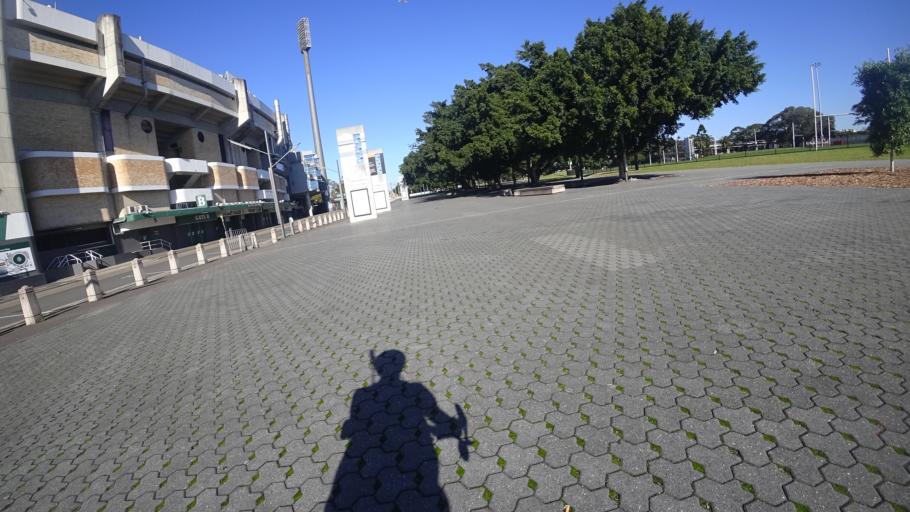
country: AU
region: New South Wales
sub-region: Woollahra
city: Paddington
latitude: -33.8914
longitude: 151.2233
